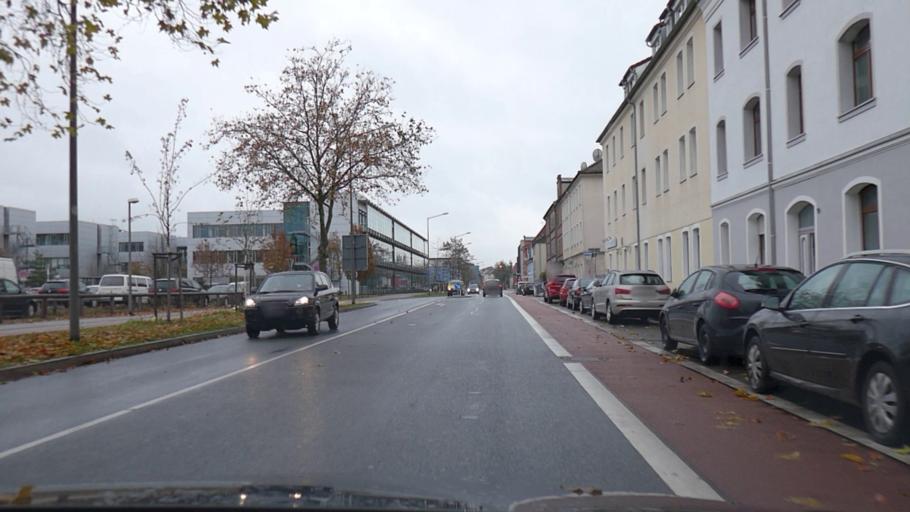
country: DE
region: Bavaria
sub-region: Regierungsbezirk Mittelfranken
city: Erlangen
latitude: 49.5960
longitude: 11.0181
